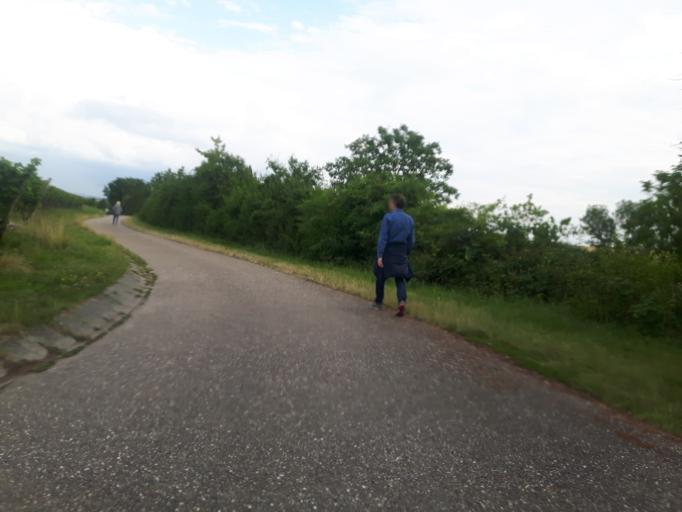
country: DE
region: Baden-Wuerttemberg
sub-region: Regierungsbezirk Stuttgart
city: Brackenheim
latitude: 49.0996
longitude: 9.0660
